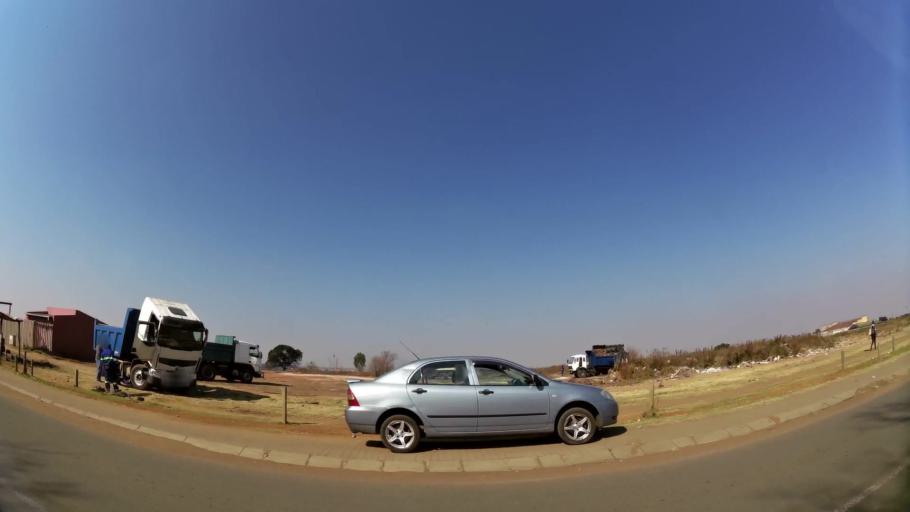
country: ZA
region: Gauteng
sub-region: Ekurhuleni Metropolitan Municipality
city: Boksburg
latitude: -26.2306
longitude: 28.2962
